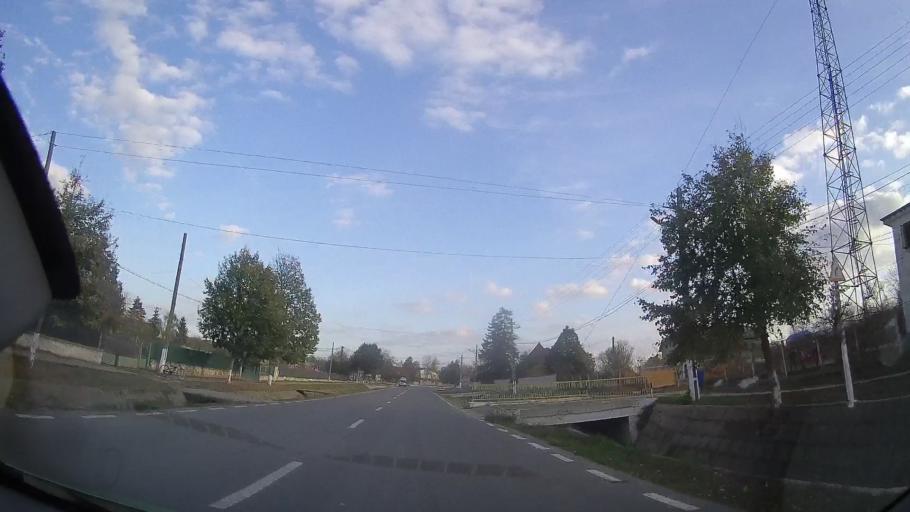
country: RO
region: Constanta
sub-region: Comuna Independenta
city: Independenta
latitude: 43.9520
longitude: 28.0815
